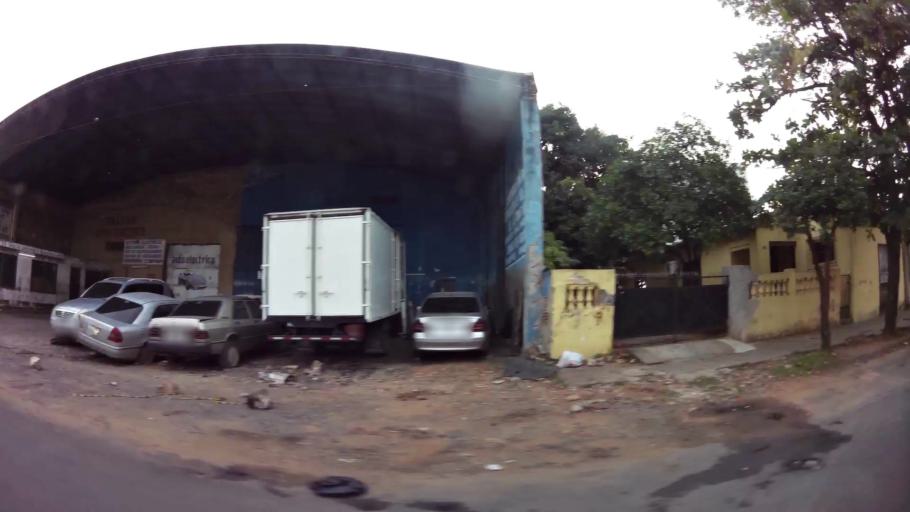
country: PY
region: Central
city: Lambare
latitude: -25.3291
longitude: -57.5751
